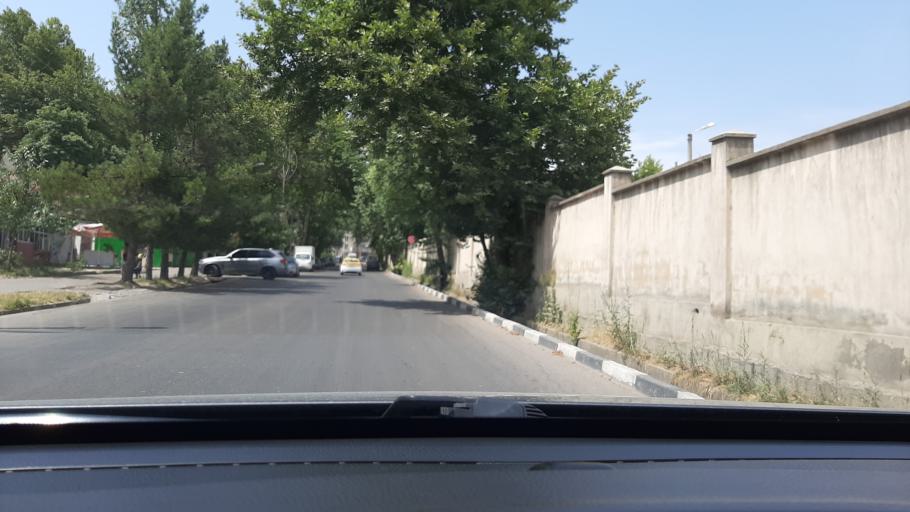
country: TJ
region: Dushanbe
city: Dushanbe
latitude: 38.5804
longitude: 68.7321
